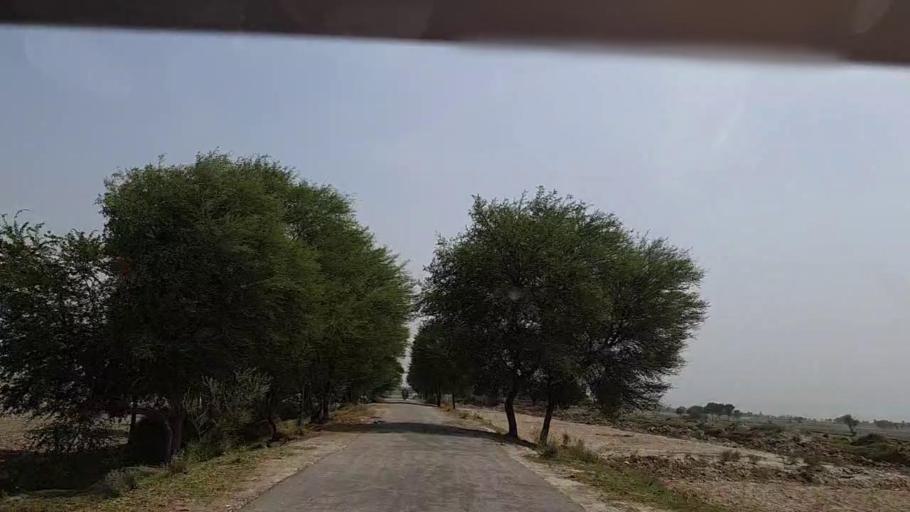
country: PK
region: Sindh
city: Khairpur Nathan Shah
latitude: 27.0723
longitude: 67.6878
